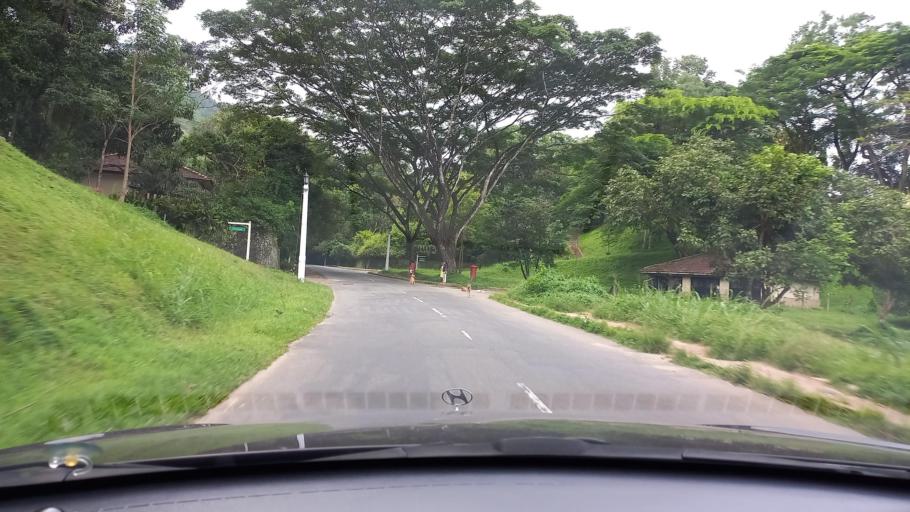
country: LK
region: Central
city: Kandy
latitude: 7.2502
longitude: 80.5976
